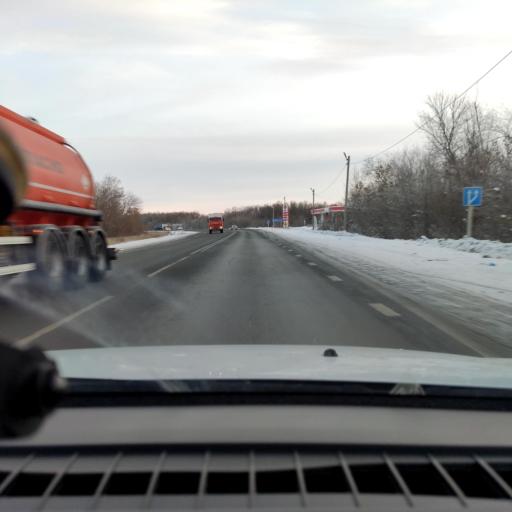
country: RU
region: Samara
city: Novokuybyshevsk
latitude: 52.9956
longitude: 49.9518
